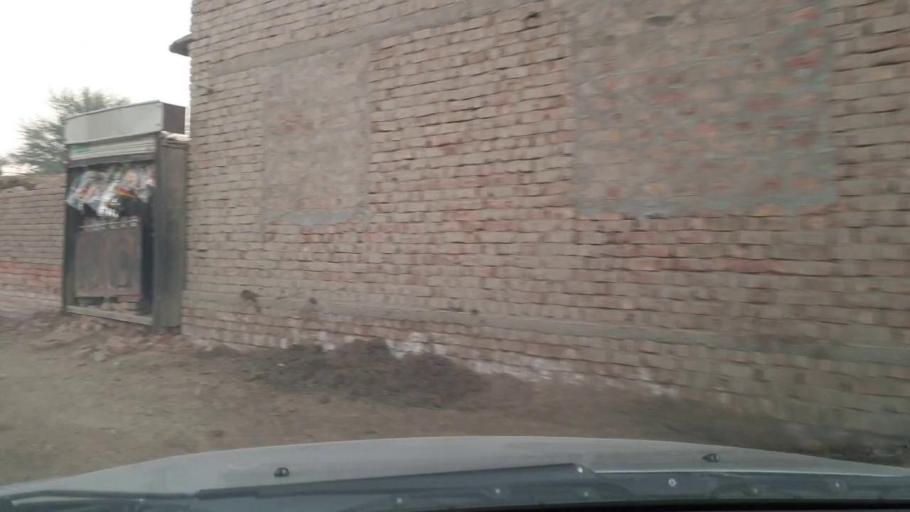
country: PK
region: Sindh
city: Mirpur Mathelo
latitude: 28.0205
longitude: 69.5200
